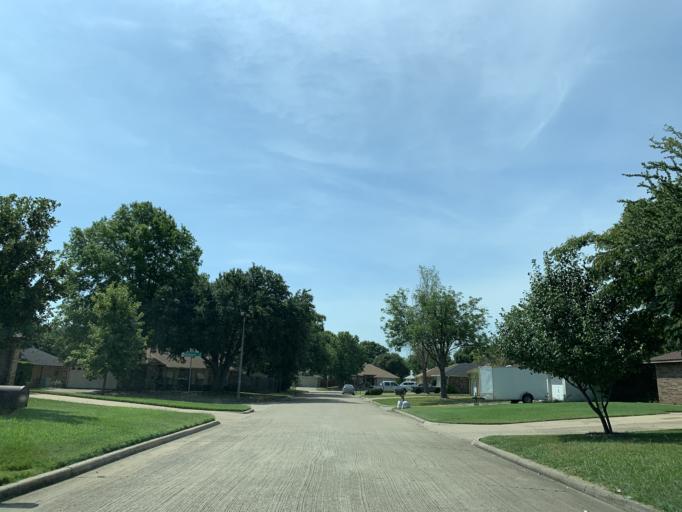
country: US
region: Texas
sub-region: Dallas County
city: Grand Prairie
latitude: 32.6692
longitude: -97.0435
